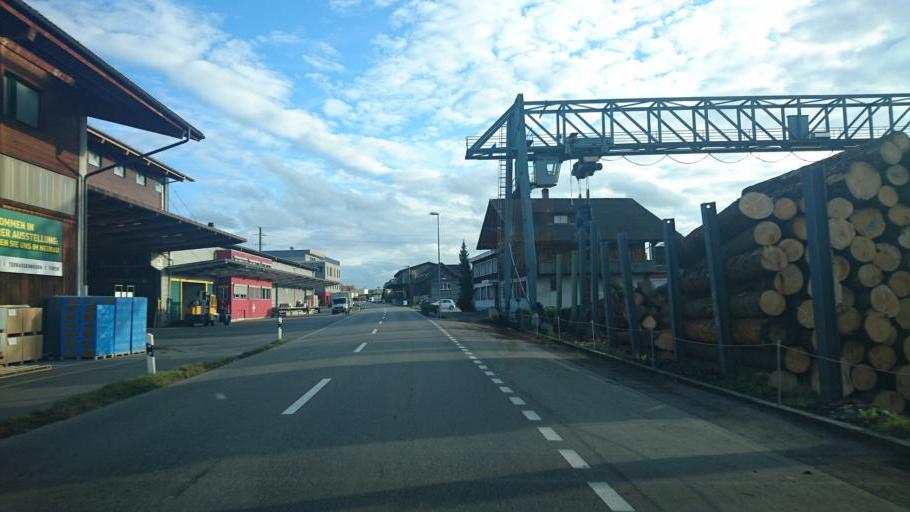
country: CH
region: Bern
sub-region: Bern-Mittelland District
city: Vechigen
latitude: 46.9404
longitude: 7.5578
